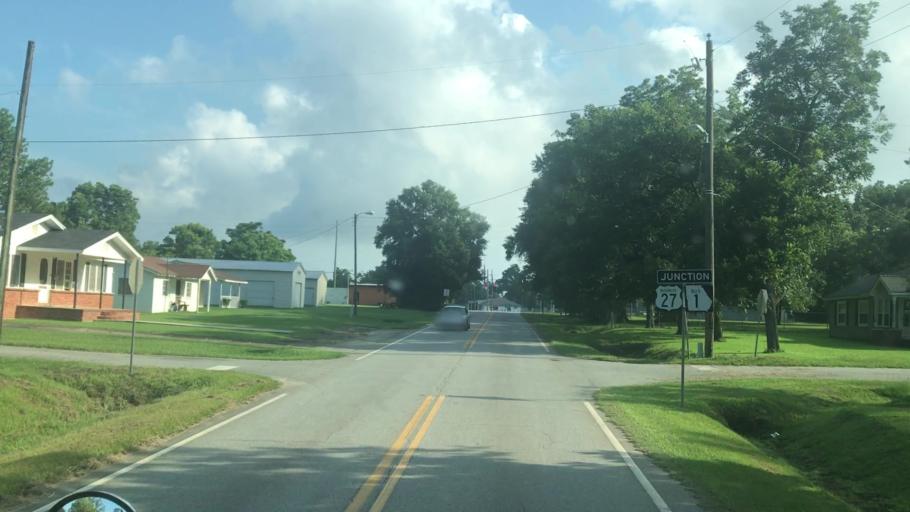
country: US
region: Florida
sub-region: Gadsden County
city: Havana
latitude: 30.7475
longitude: -84.4839
